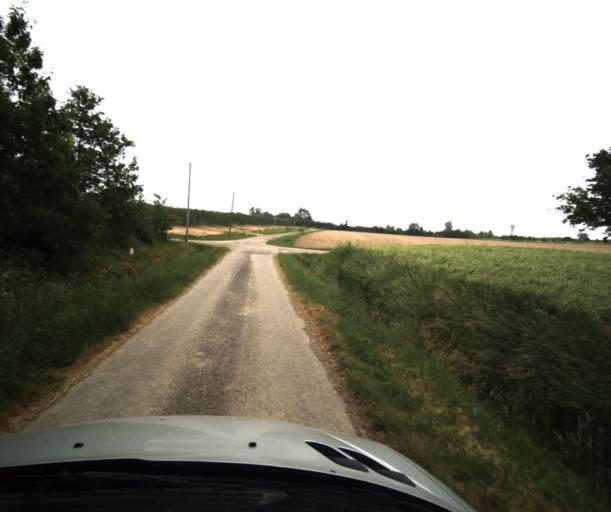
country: FR
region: Midi-Pyrenees
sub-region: Departement du Tarn-et-Garonne
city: Saint-Nicolas-de-la-Grave
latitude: 44.0531
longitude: 0.9905
